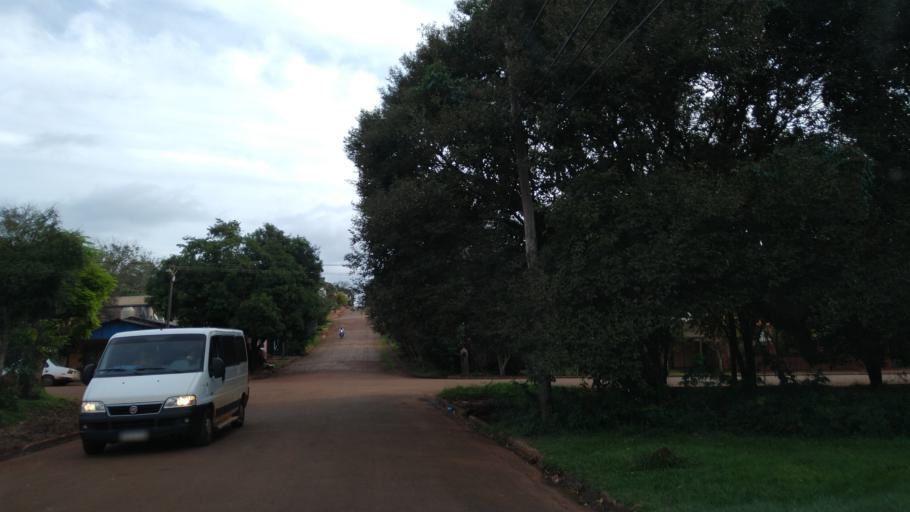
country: AR
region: Misiones
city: Jardin America
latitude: -27.0422
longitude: -55.2370
